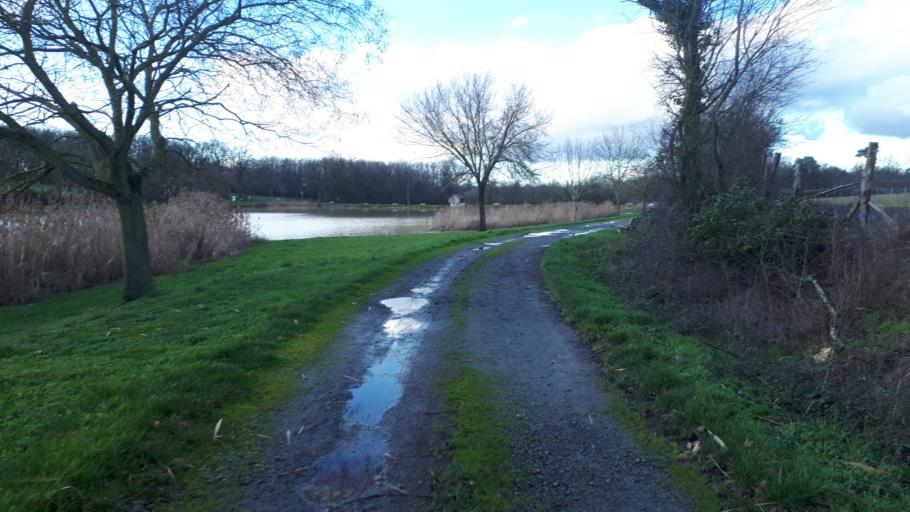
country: FR
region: Poitou-Charentes
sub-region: Departement de la Vienne
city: Pleumartin
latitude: 46.6362
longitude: 0.7648
